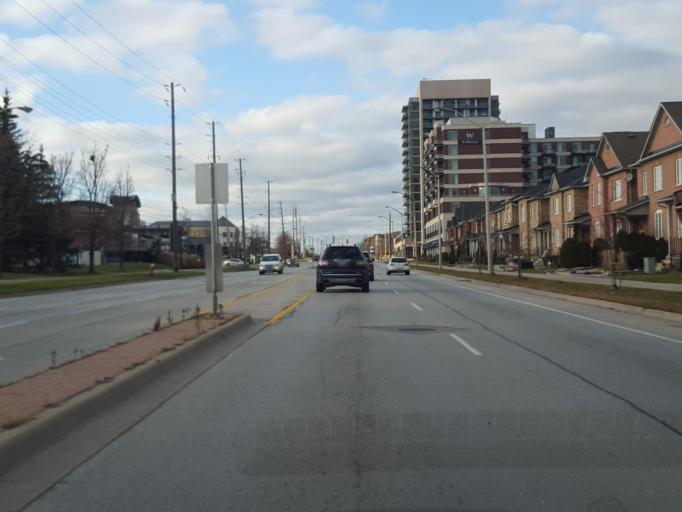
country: CA
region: Ontario
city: Burlington
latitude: 43.3909
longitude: -79.7862
